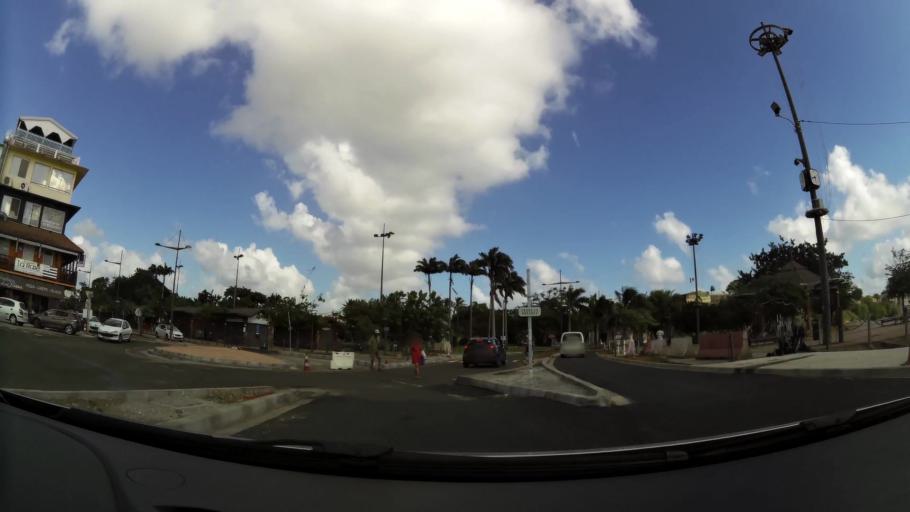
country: MQ
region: Martinique
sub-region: Martinique
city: Fort-de-France
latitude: 14.6025
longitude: -61.0692
